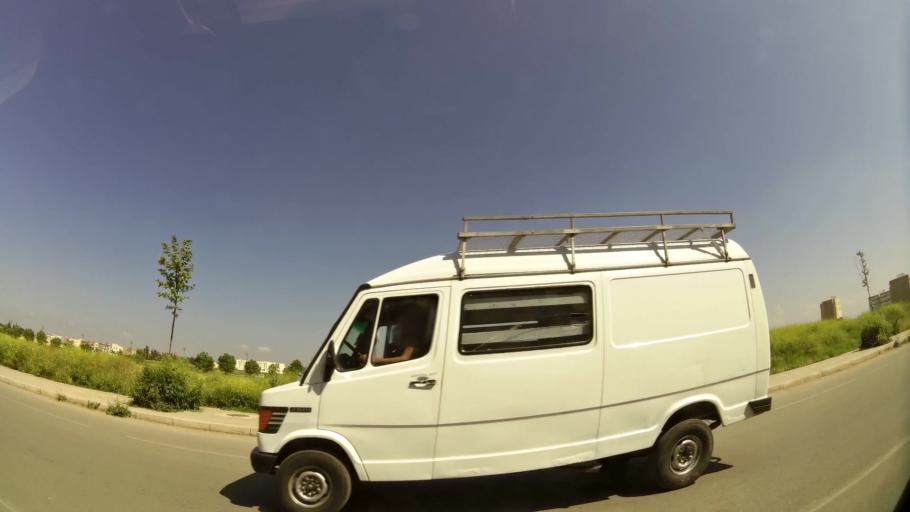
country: MA
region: Fes-Boulemane
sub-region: Fes
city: Fes
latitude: 34.0133
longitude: -5.0218
